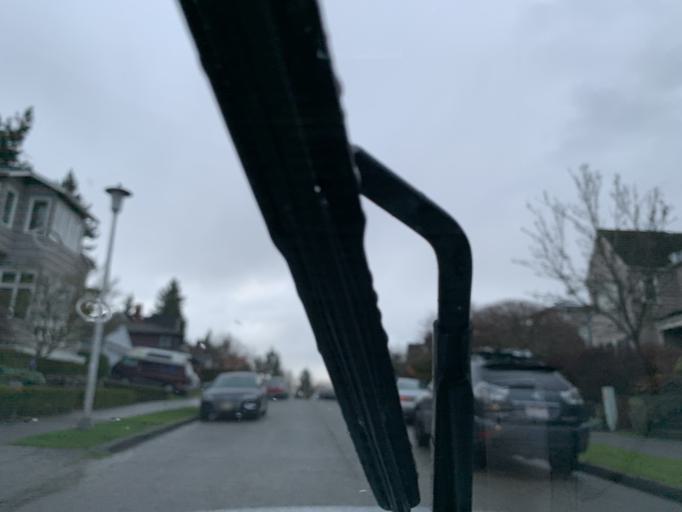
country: US
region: Washington
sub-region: King County
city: Yarrow Point
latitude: 47.6615
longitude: -122.2725
